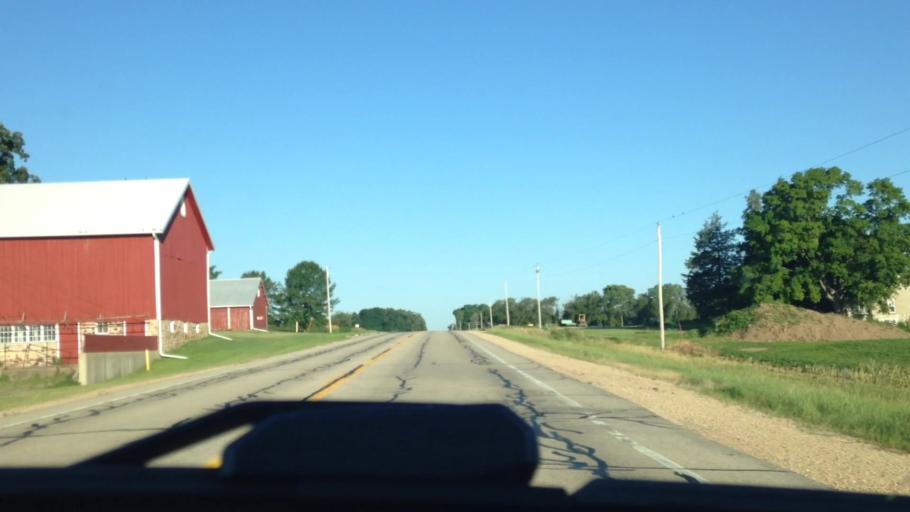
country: US
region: Wisconsin
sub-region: Columbia County
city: Fall River
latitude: 43.3416
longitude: -89.0622
